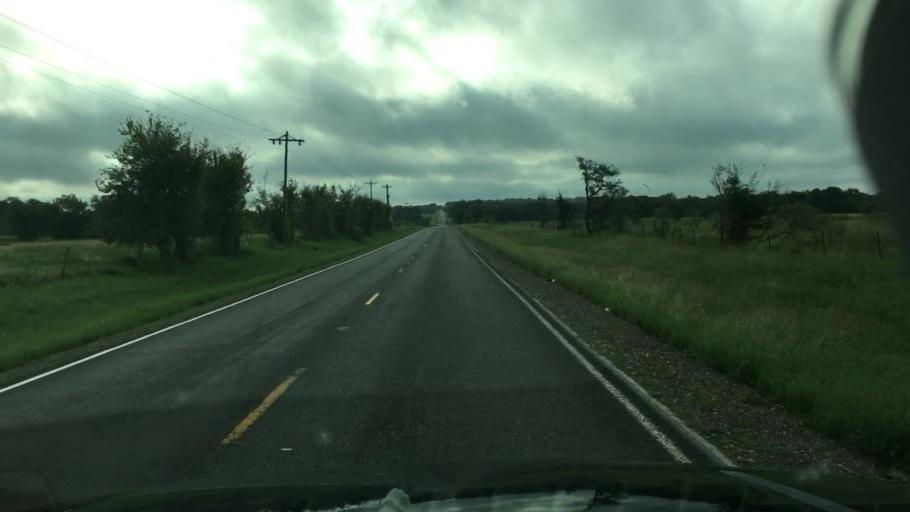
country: US
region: Texas
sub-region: Lee County
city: Lexington
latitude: 30.3740
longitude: -96.8458
